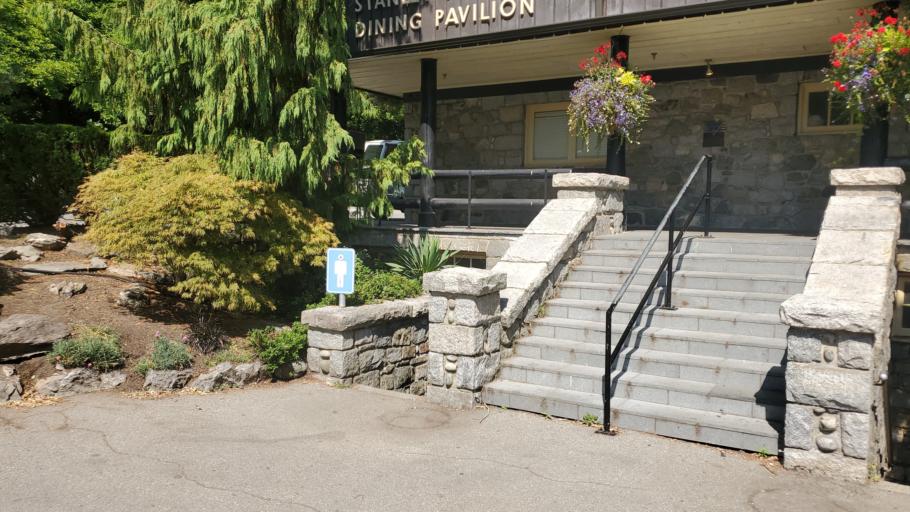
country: CA
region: British Columbia
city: West End
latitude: 49.2995
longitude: -123.1340
